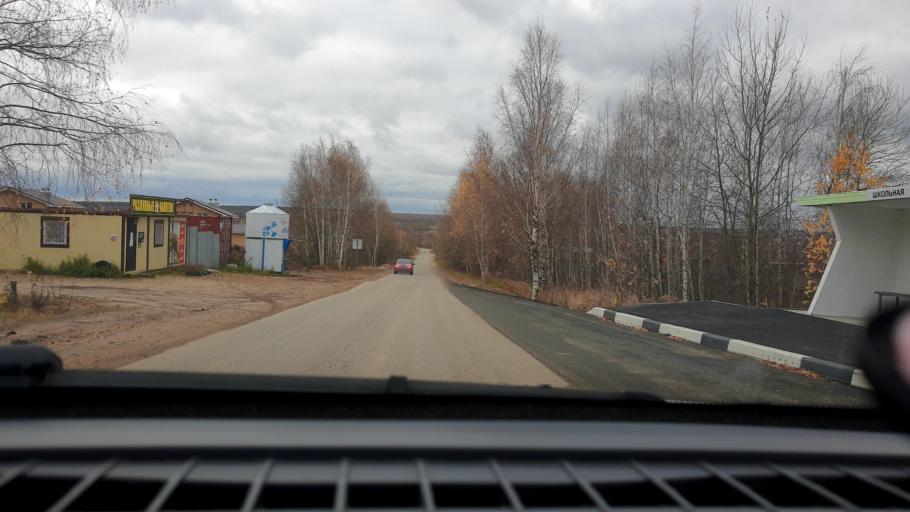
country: RU
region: Nizjnij Novgorod
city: Afonino
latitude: 56.2035
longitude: 44.1386
